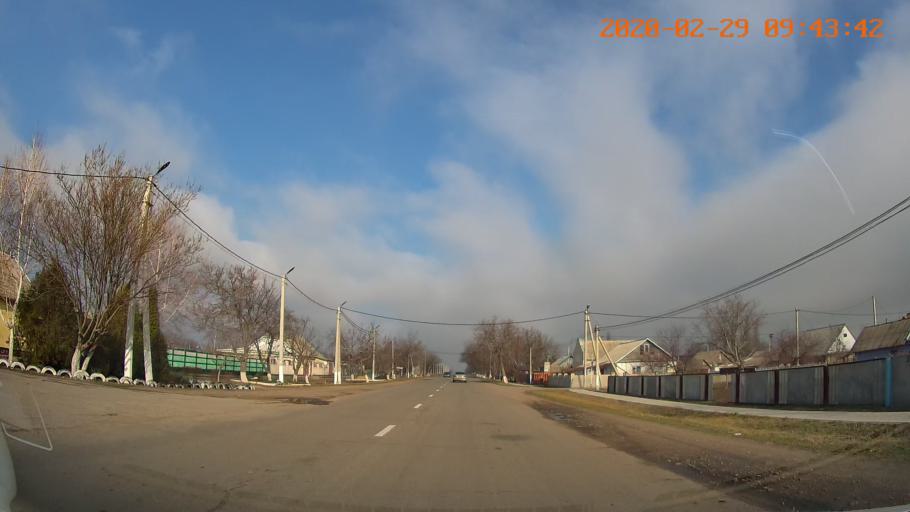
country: MD
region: Telenesti
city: Crasnoe
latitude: 46.6463
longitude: 29.8205
